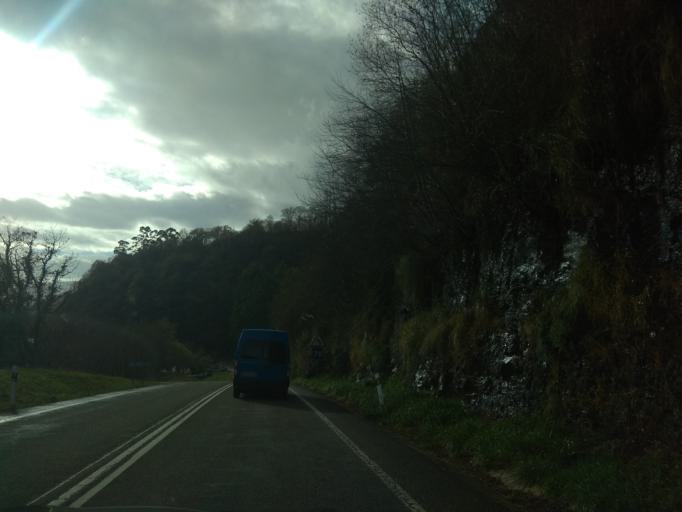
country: ES
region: Cantabria
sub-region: Provincia de Cantabria
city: San Pedro del Romeral
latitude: 43.1478
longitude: -3.8988
